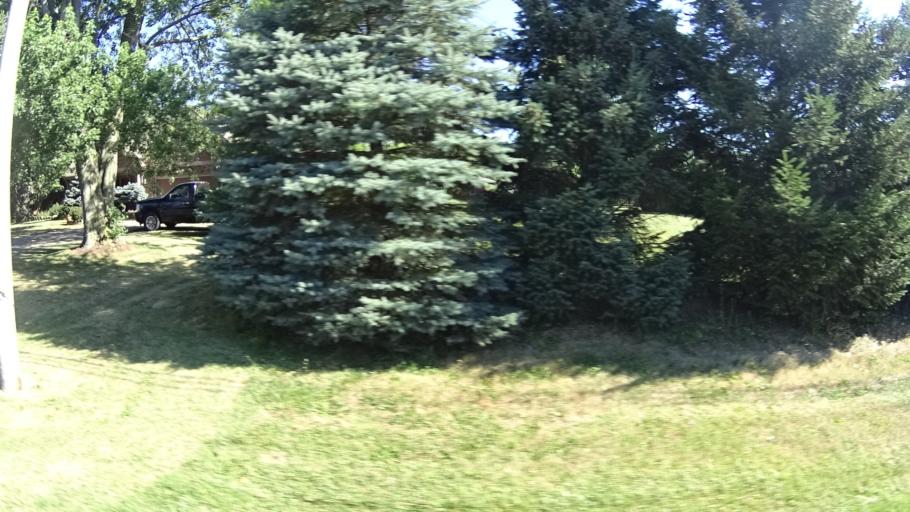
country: US
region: Ohio
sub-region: Erie County
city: Sandusky
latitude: 41.4096
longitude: -82.7335
